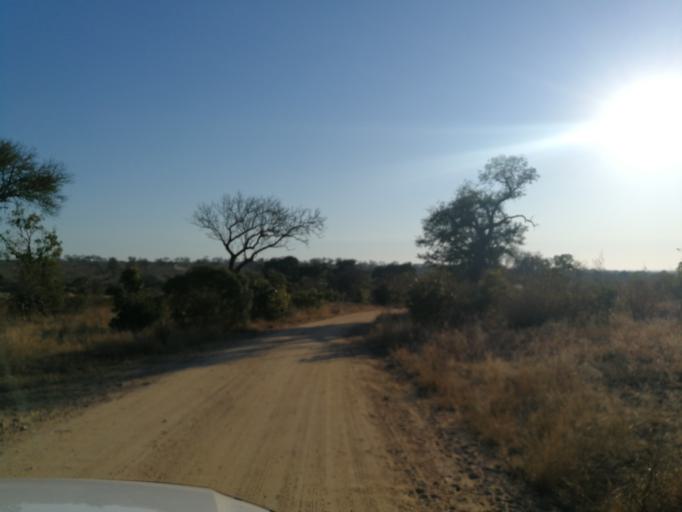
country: ZA
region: Limpopo
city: Thulamahashi
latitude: -25.0122
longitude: 31.4296
